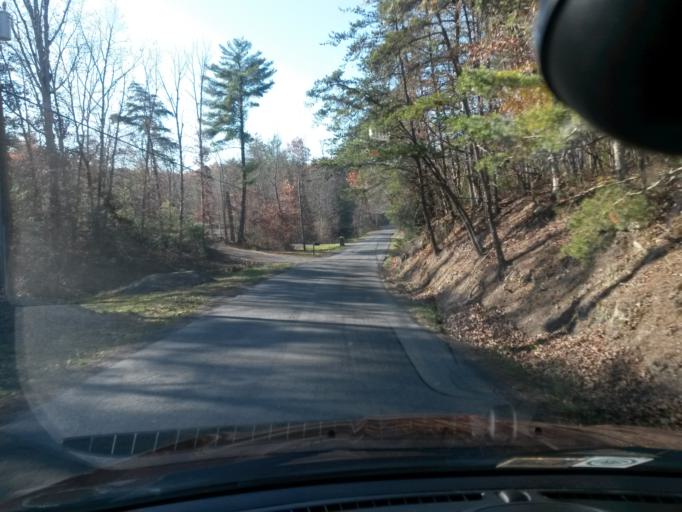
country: US
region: Virginia
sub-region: Alleghany County
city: Clifton Forge
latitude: 37.8016
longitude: -79.7469
